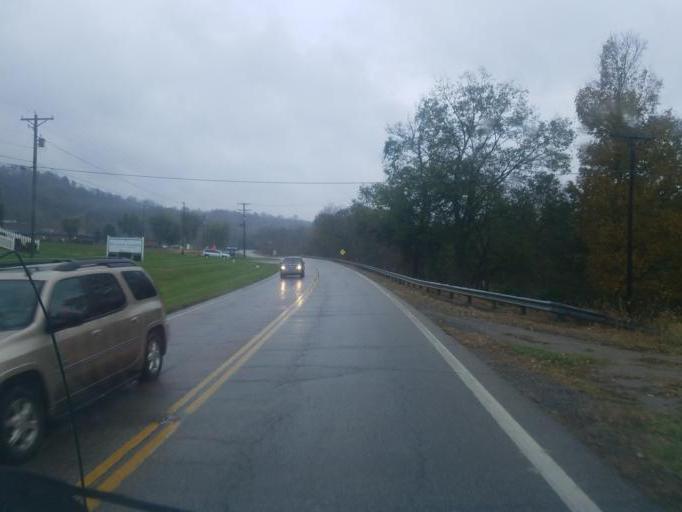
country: US
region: Ohio
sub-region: Morgan County
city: McConnelsville
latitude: 39.6117
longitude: -81.8229
